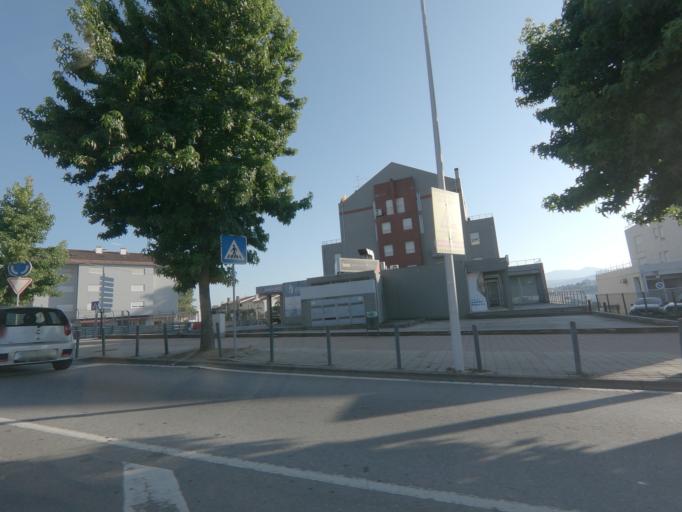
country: PT
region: Vila Real
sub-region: Vila Real
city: Vila Real
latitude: 41.3079
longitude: -7.7252
